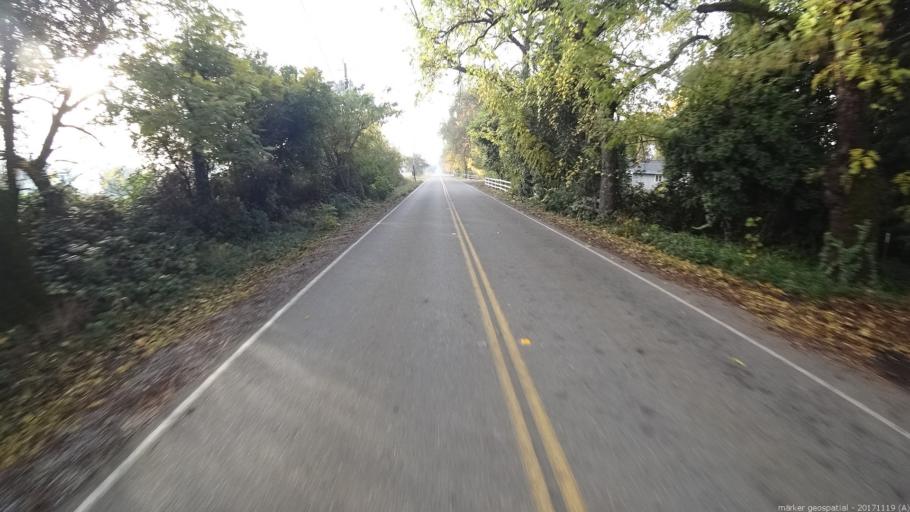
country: US
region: California
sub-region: Shasta County
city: Anderson
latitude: 40.4896
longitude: -122.3170
